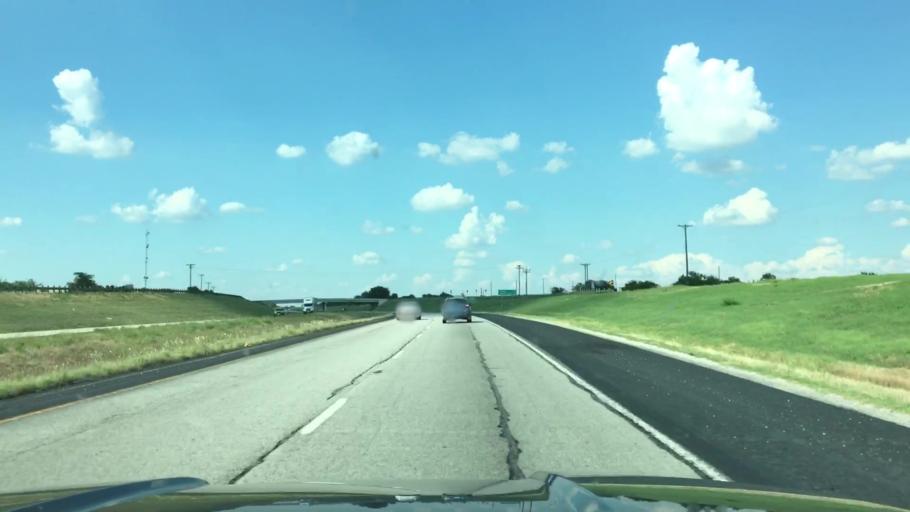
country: US
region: Texas
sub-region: Wise County
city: Rhome
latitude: 33.0656
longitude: -97.4746
